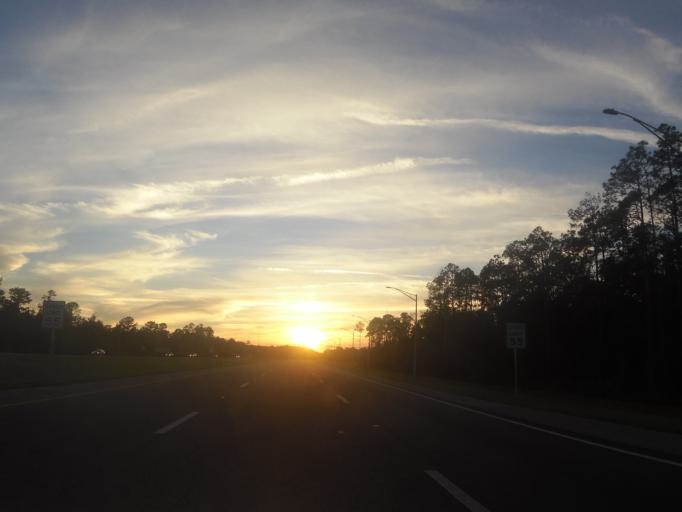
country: US
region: Florida
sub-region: Saint Johns County
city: Palm Valley
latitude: 30.1073
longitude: -81.4556
